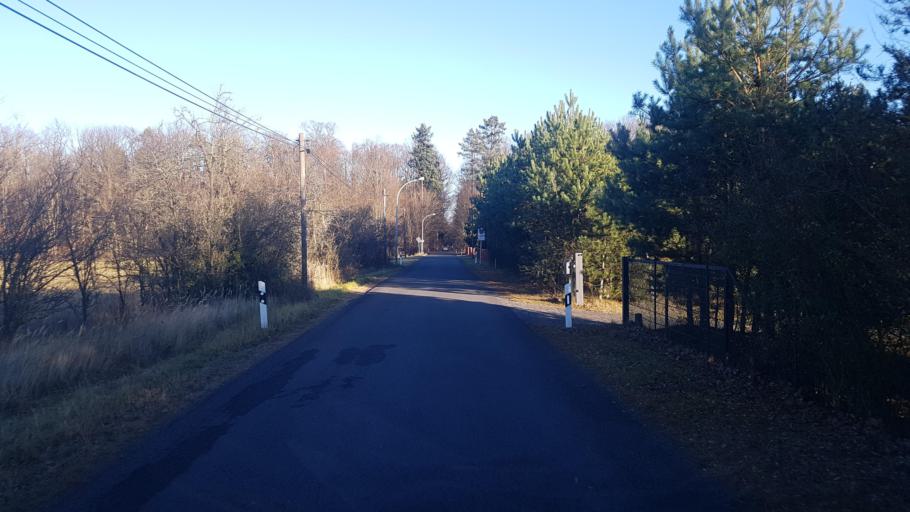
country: DE
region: Brandenburg
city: Tauer
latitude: 51.9359
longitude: 14.4701
